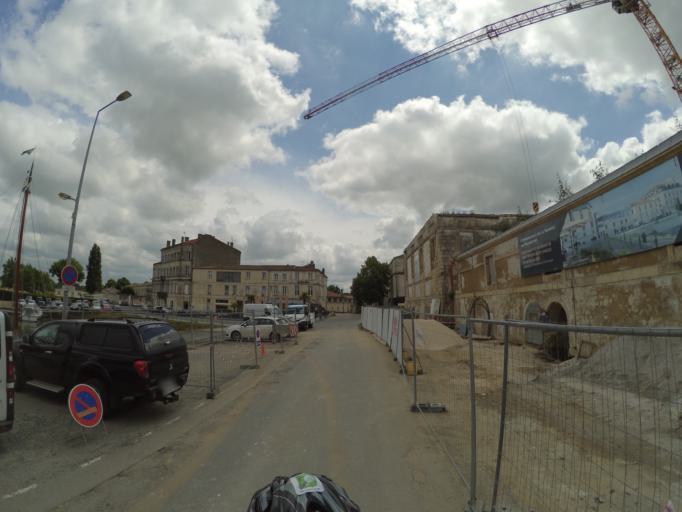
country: FR
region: Poitou-Charentes
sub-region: Departement de la Charente-Maritime
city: Rochefort
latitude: 45.9422
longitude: -0.9568
